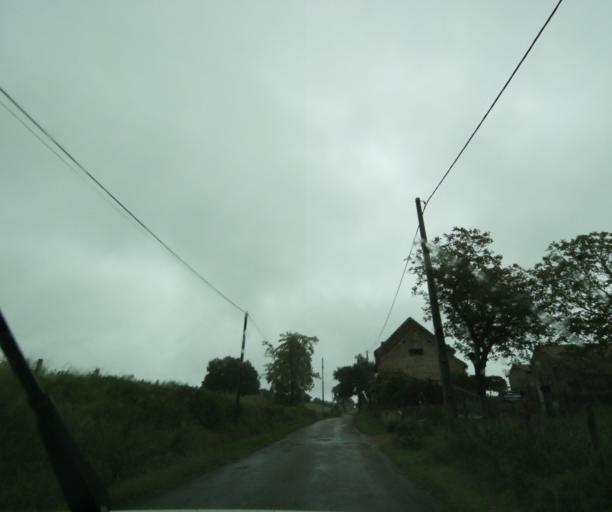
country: FR
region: Bourgogne
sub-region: Departement de Saone-et-Loire
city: Charolles
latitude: 46.3651
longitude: 4.2494
